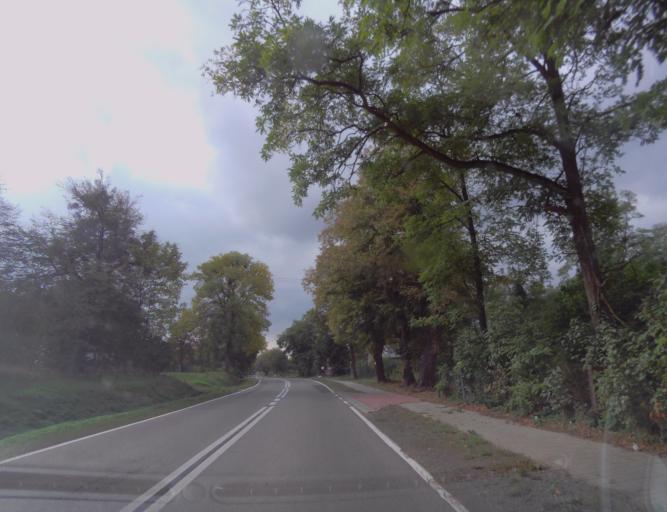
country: PL
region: Lublin Voivodeship
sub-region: Powiat krasnostawski
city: Rudnik
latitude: 50.9293
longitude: 22.9161
